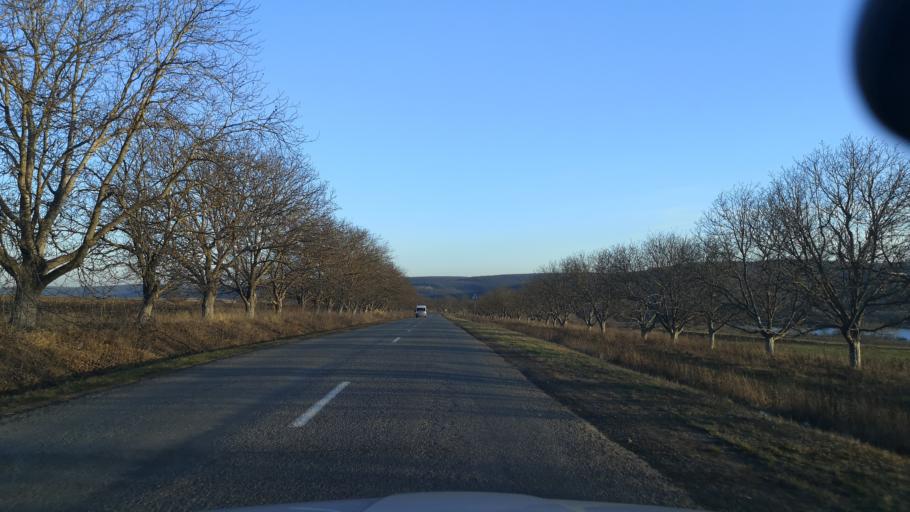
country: MD
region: Orhei
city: Orhei
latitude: 47.2871
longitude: 28.8224
